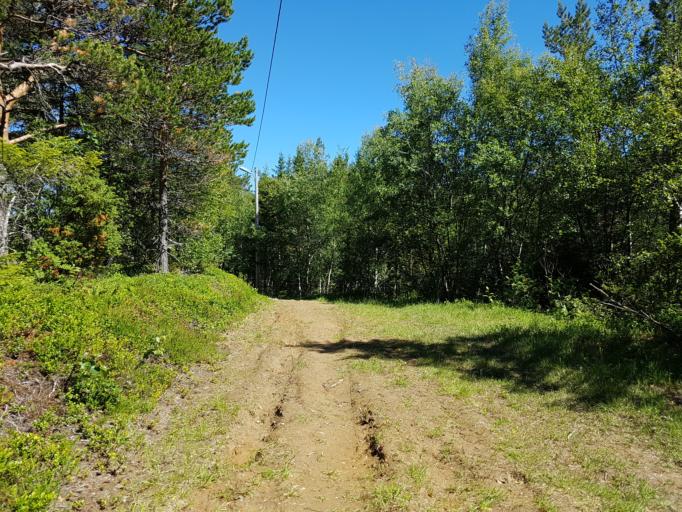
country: NO
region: Sor-Trondelag
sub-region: Skaun
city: Borsa
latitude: 63.4324
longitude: 10.1885
